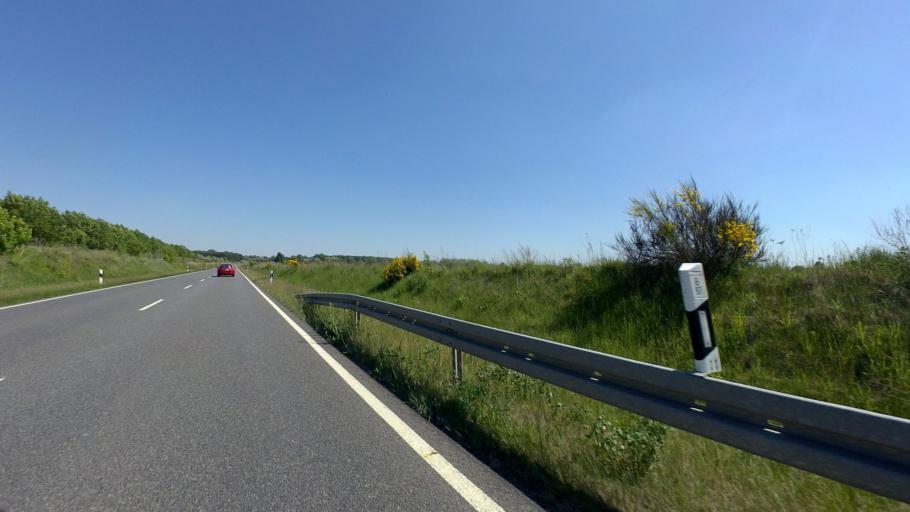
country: DE
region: Brandenburg
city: Spremberg
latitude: 51.5701
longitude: 14.3337
